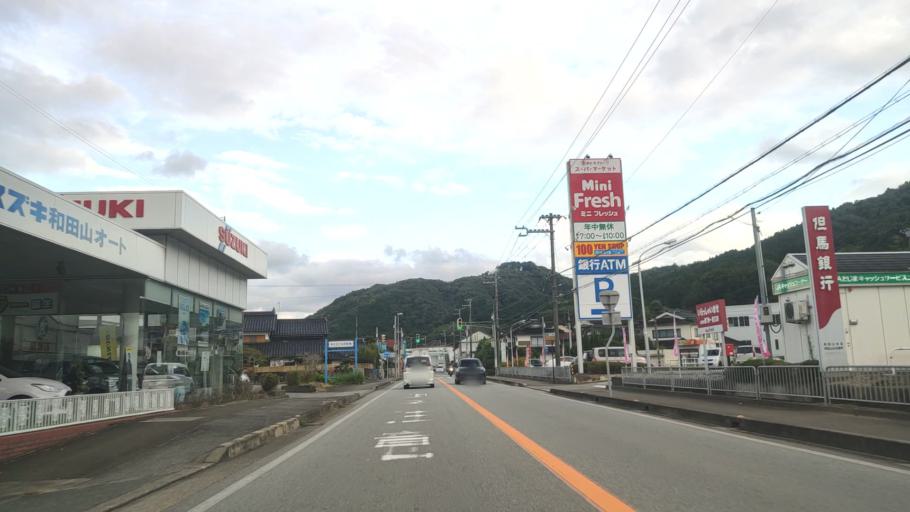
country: JP
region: Hyogo
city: Toyooka
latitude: 35.3583
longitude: 134.8229
